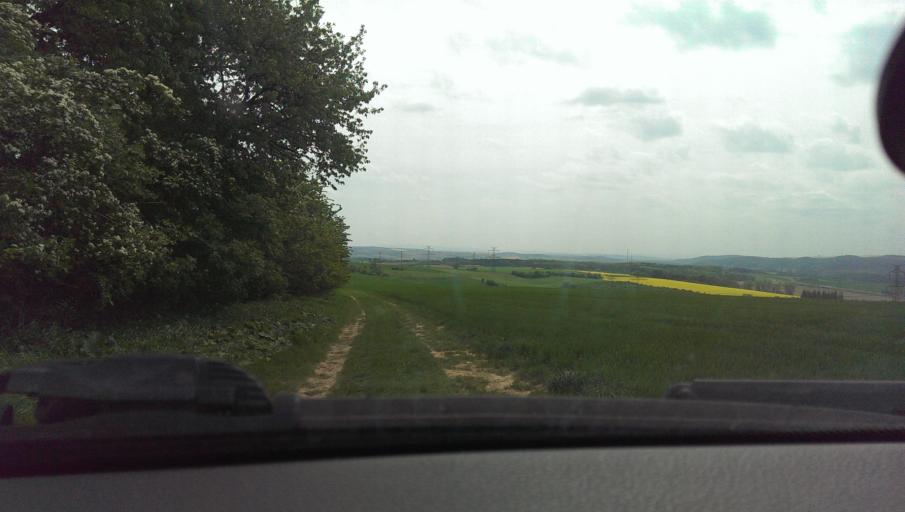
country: CZ
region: Zlin
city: Tlumacov
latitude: 49.2653
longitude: 17.5297
